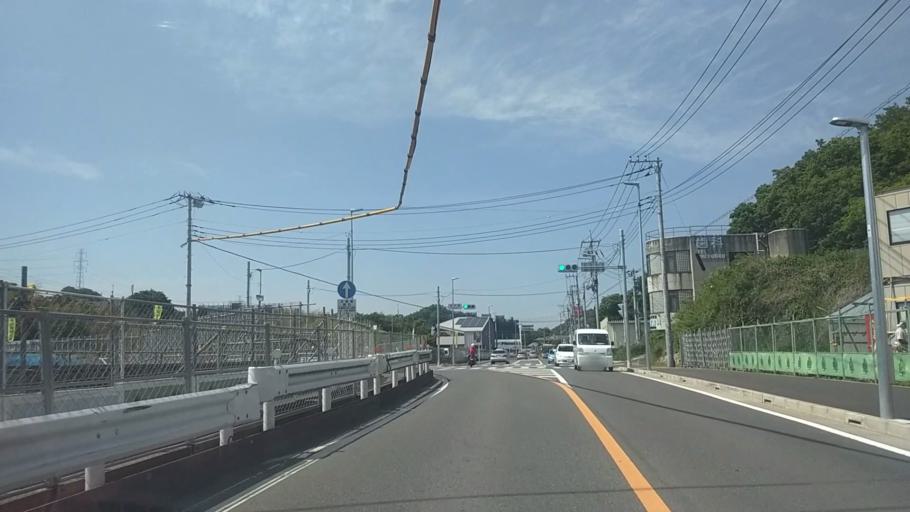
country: JP
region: Kanagawa
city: Kamakura
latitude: 35.3515
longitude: 139.5802
